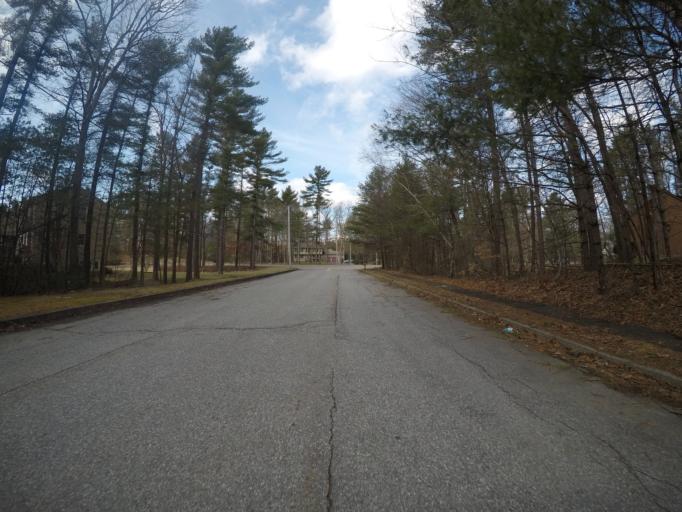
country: US
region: Massachusetts
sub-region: Bristol County
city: Easton
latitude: 42.0033
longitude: -71.1457
